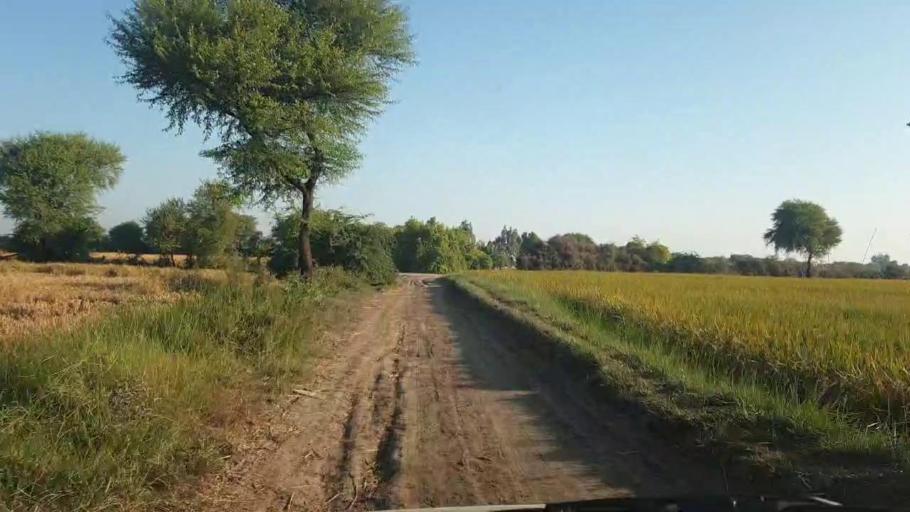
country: PK
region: Sindh
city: Talhar
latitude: 24.8022
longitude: 68.8191
